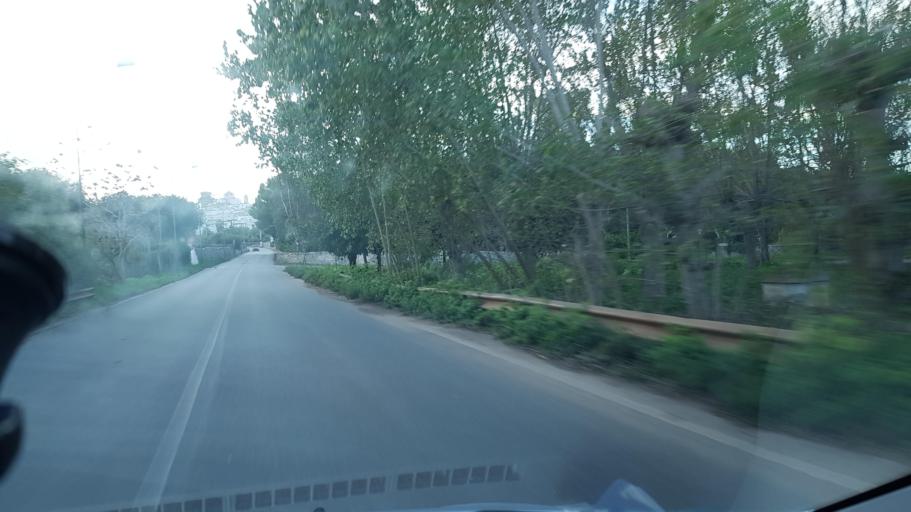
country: IT
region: Apulia
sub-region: Provincia di Brindisi
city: Ceglie Messapica
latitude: 40.6452
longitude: 17.5282
